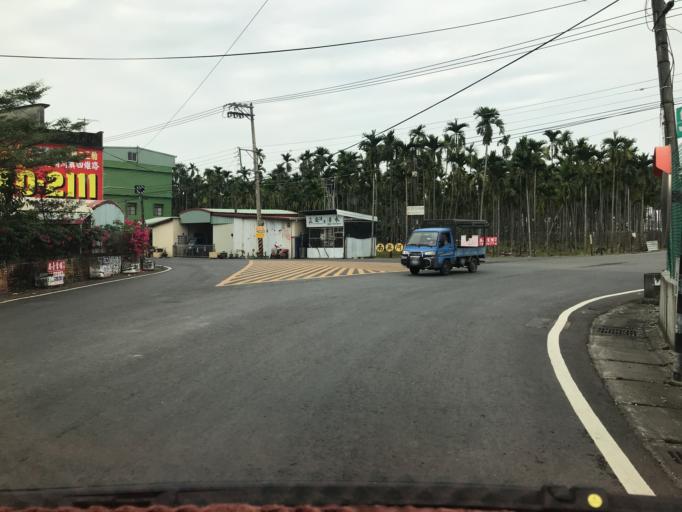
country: TW
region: Taiwan
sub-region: Pingtung
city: Pingtung
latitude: 22.5349
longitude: 120.5582
